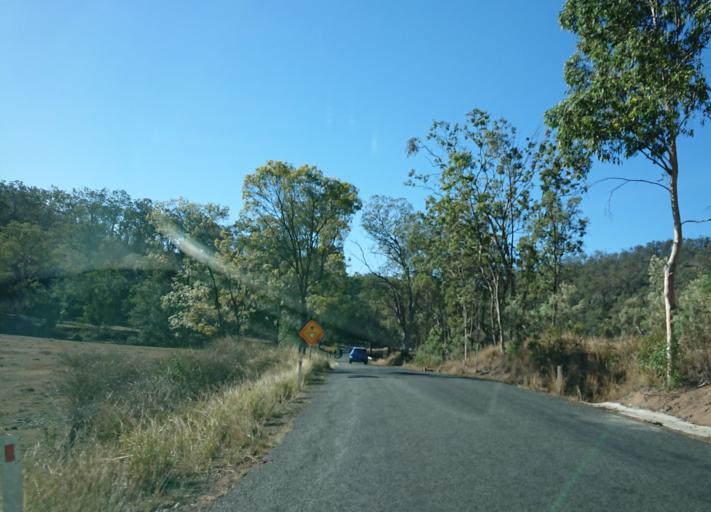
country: AU
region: Queensland
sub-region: Toowoomba
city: Top Camp
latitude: -27.7602
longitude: 152.0819
